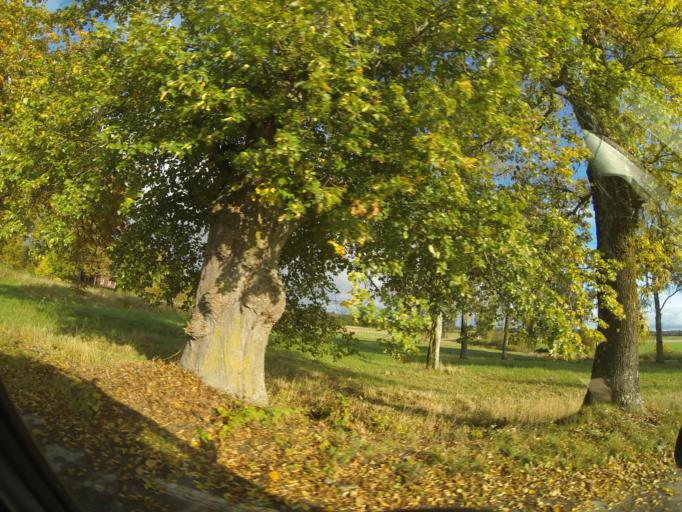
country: SE
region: Soedermanland
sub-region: Eskilstuna Kommun
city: Kvicksund
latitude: 59.3414
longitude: 16.2535
